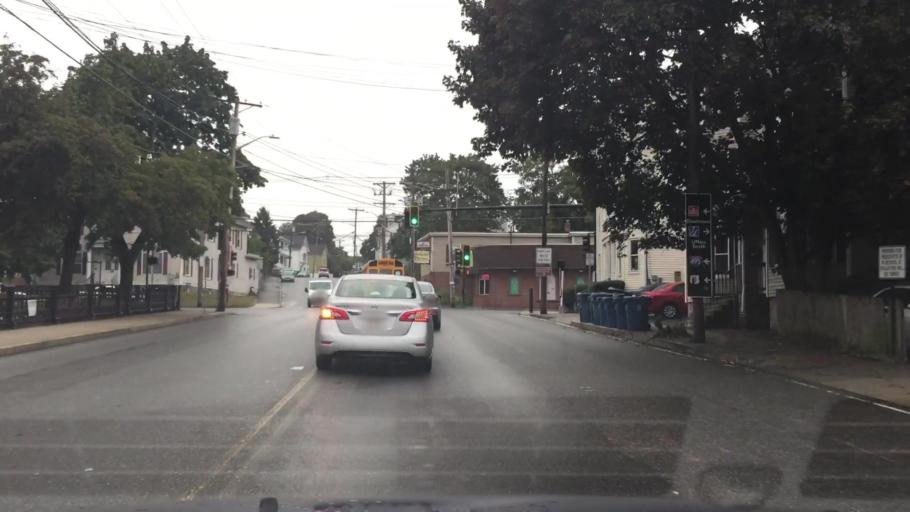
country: US
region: Massachusetts
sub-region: Middlesex County
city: Lowell
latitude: 42.6492
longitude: -71.3300
